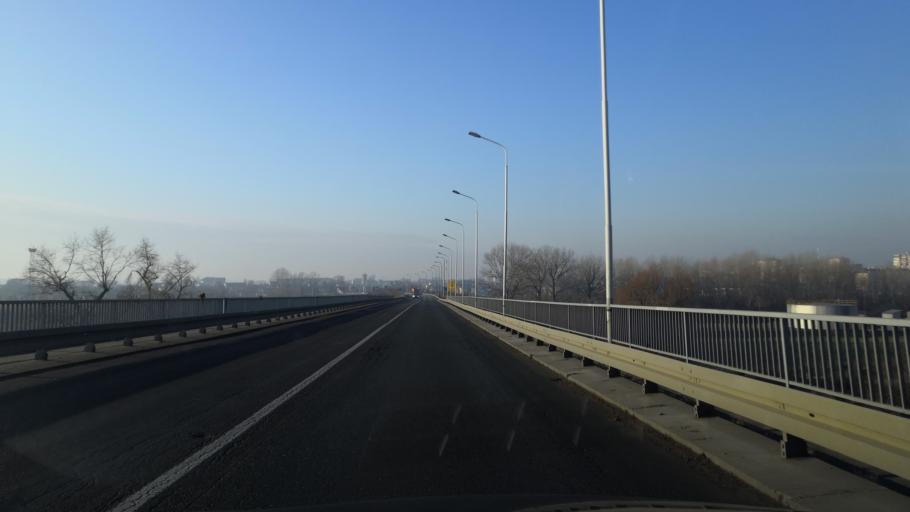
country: RS
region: Central Serbia
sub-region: Macvanski Okrug
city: Sabac
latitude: 44.7569
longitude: 19.7119
